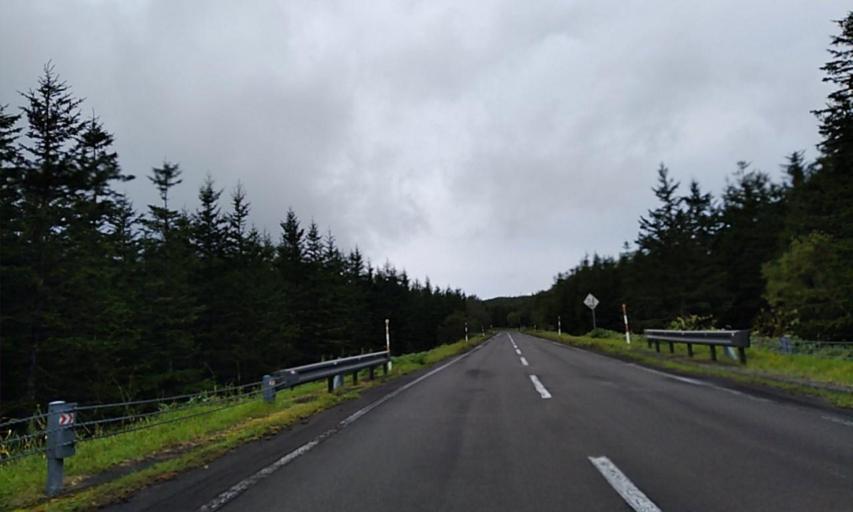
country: JP
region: Hokkaido
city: Abashiri
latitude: 43.6079
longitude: 144.5909
